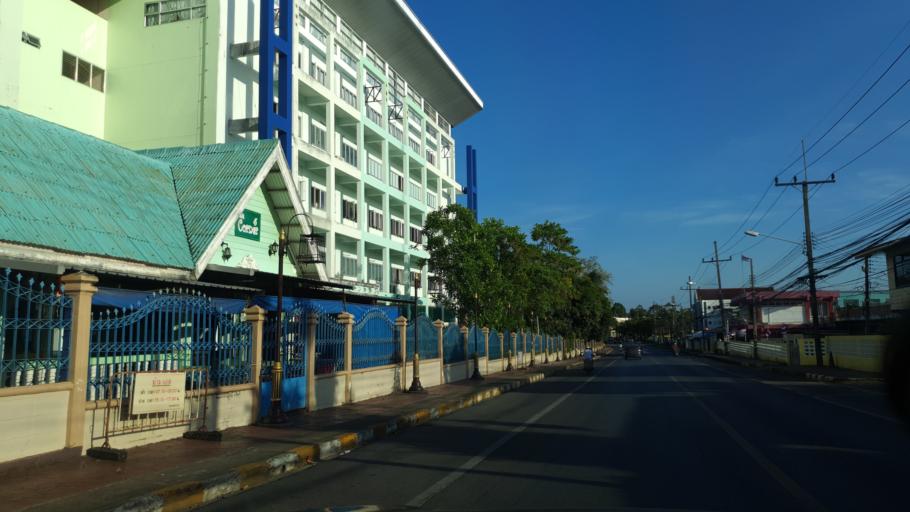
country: TH
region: Krabi
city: Krabi
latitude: 8.0578
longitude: 98.9135
